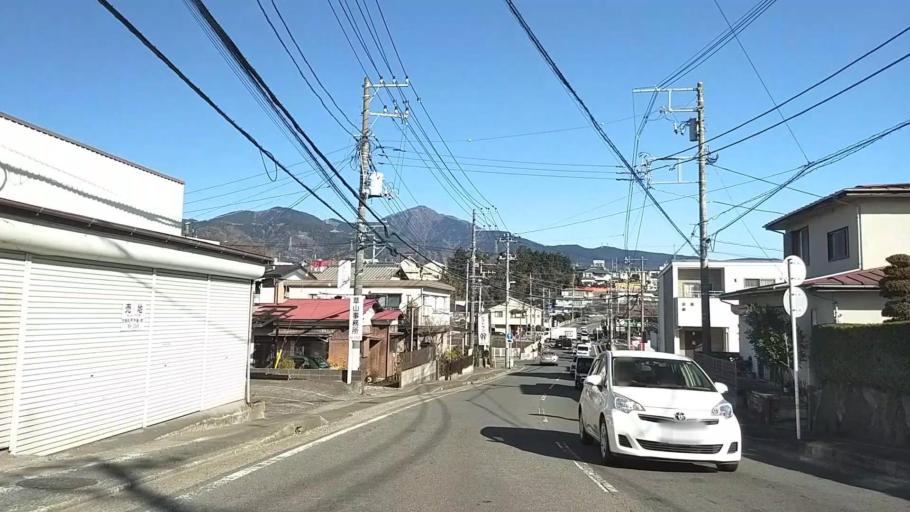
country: JP
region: Kanagawa
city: Hadano
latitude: 35.3769
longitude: 139.2081
